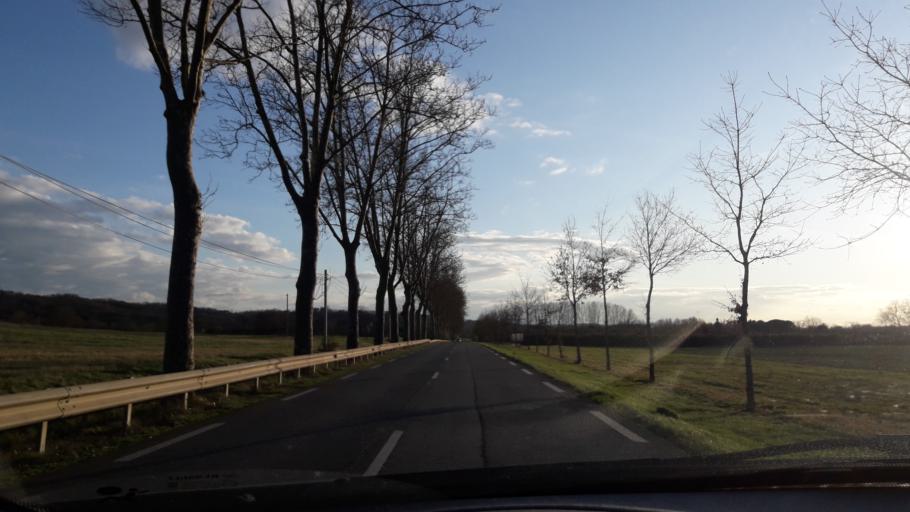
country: FR
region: Midi-Pyrenees
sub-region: Departement de la Haute-Garonne
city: Montaigut-sur-Save
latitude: 43.7057
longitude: 1.2428
